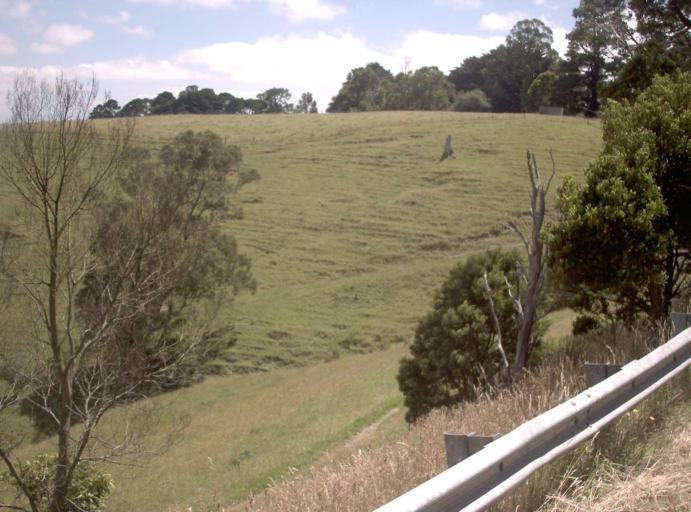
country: AU
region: Victoria
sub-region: Baw Baw
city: Warragul
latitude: -38.3023
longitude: 145.8982
